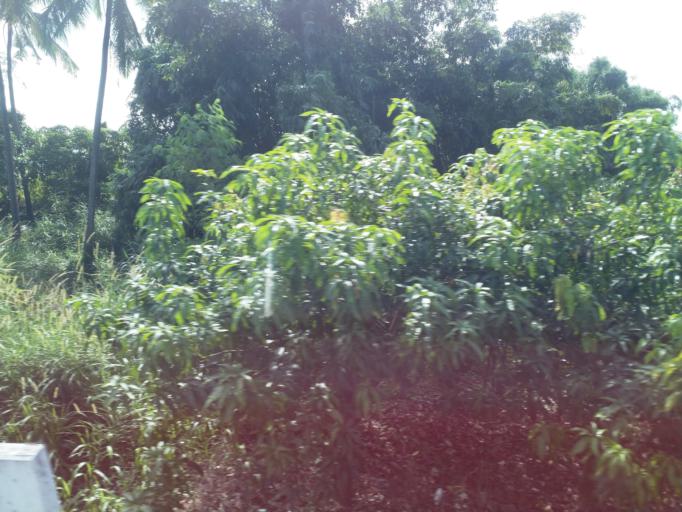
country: TW
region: Taiwan
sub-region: Pingtung
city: Pingtung
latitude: 22.8902
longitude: 120.5070
